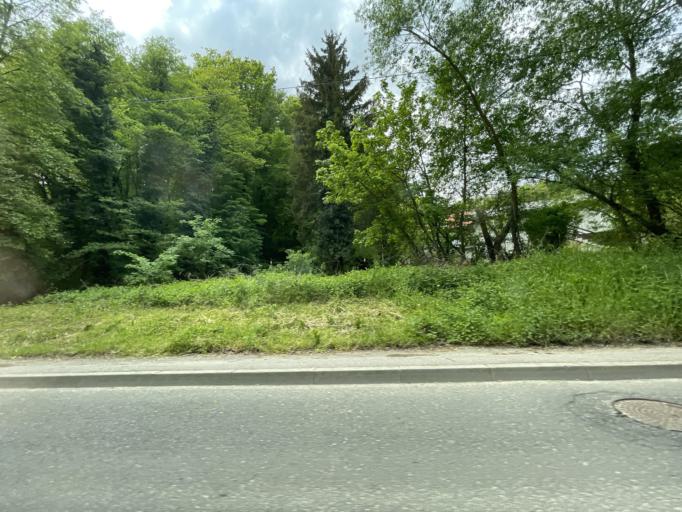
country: HR
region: Grad Zagreb
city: Zagreb
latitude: 45.8296
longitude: 15.9446
